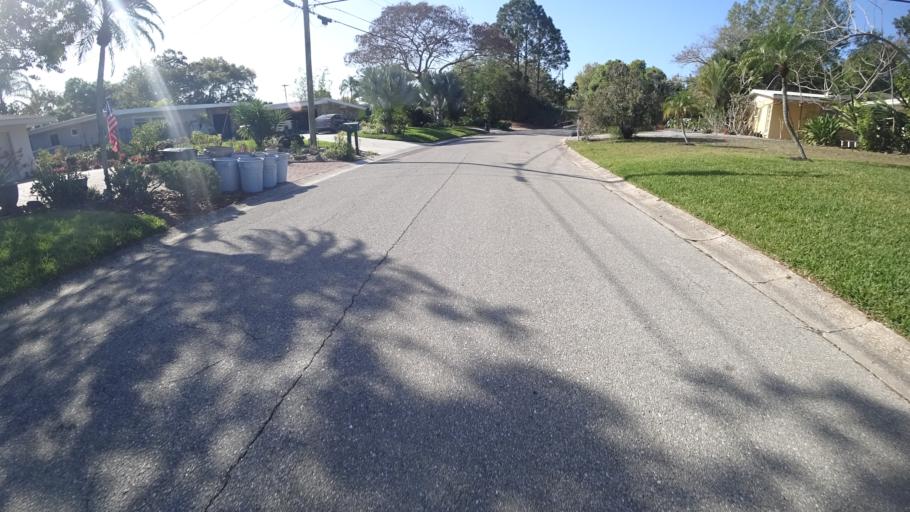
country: US
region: Florida
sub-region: Manatee County
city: Whitfield
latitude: 27.4172
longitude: -82.5570
